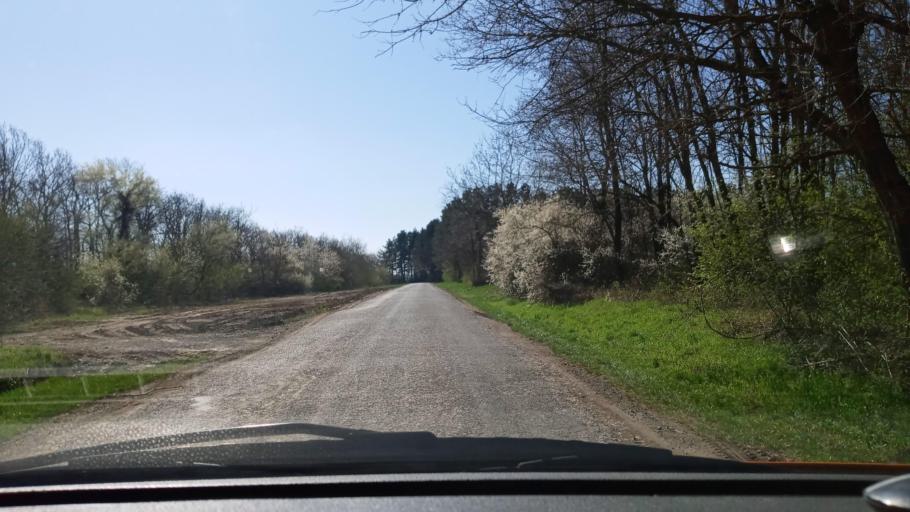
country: HU
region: Baranya
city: Kozarmisleny
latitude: 46.0782
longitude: 18.3503
